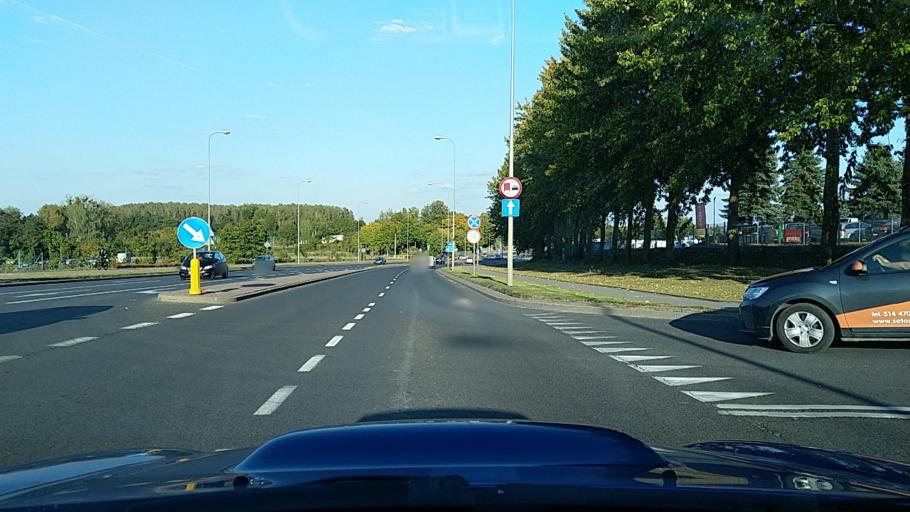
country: PL
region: Warmian-Masurian Voivodeship
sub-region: Olsztyn
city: Kortowo
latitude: 53.7706
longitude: 20.4405
